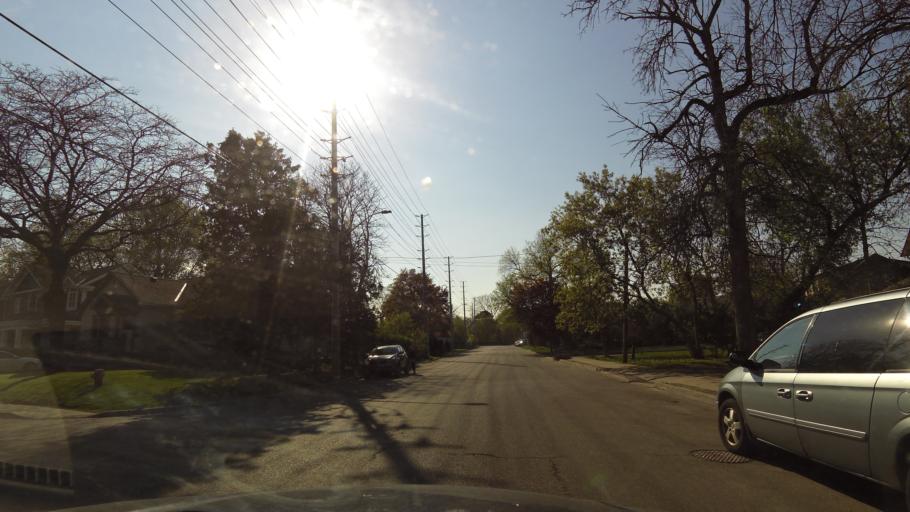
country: CA
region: Ontario
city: Mississauga
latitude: 43.5633
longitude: -79.5761
